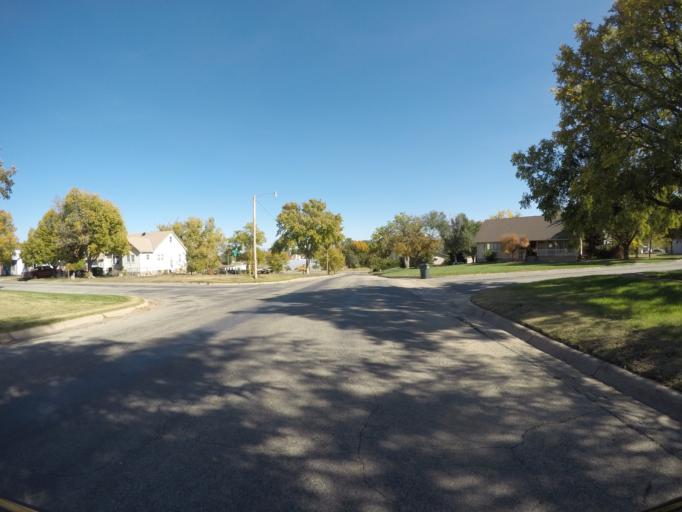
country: US
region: Kansas
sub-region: Phillips County
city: Phillipsburg
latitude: 39.7547
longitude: -99.3165
